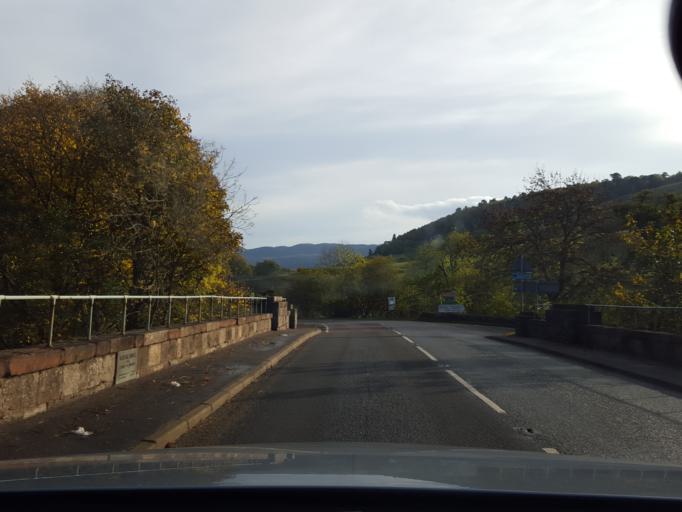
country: GB
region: Scotland
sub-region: Highland
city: Beauly
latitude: 57.3281
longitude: -4.4720
